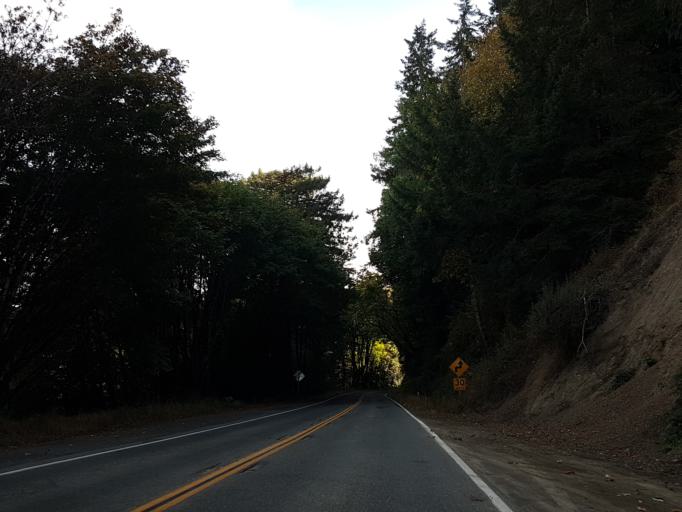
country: US
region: California
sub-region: Humboldt County
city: Rio Dell
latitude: 40.4224
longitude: -123.9785
